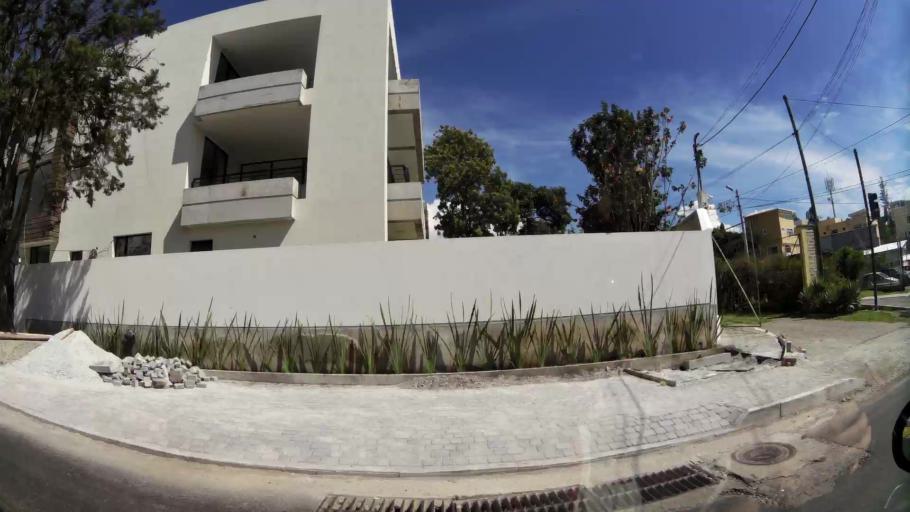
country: EC
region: Pichincha
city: Quito
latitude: -0.1981
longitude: -78.4275
